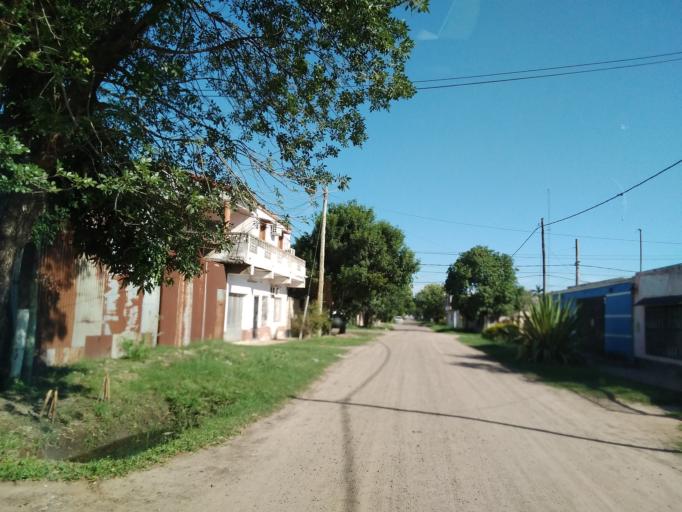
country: AR
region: Corrientes
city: Corrientes
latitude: -27.4834
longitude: -58.8032
